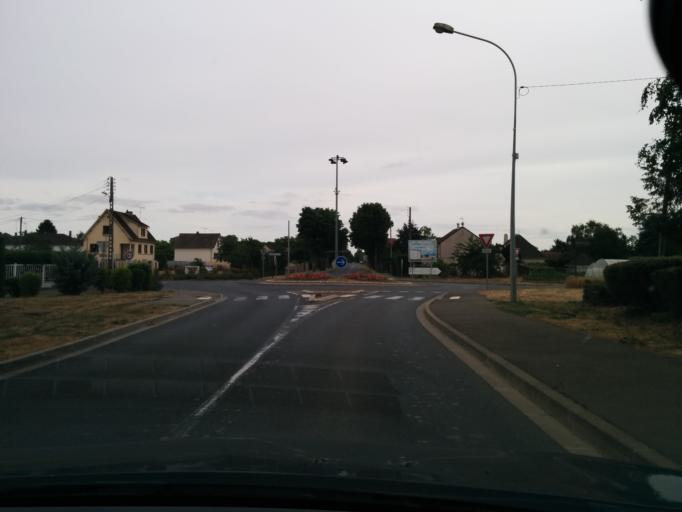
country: FR
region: Ile-de-France
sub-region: Departement de l'Essonne
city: Pussay
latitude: 48.3523
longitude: 1.9854
